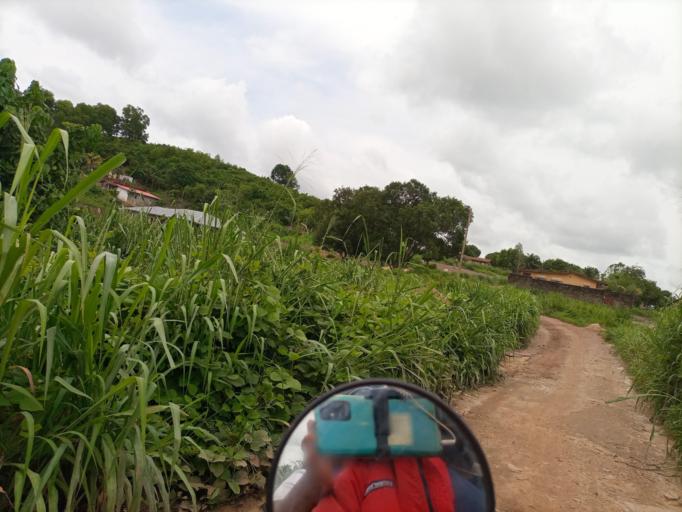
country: SL
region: Southern Province
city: Bo
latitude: 7.9480
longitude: -11.7469
